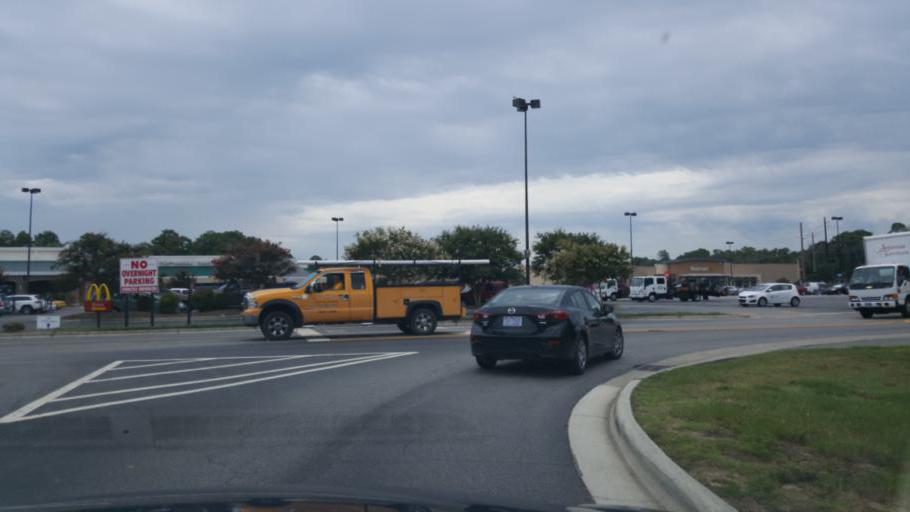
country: US
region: North Carolina
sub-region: Dare County
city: Kitty Hawk
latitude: 36.0984
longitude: -75.7204
